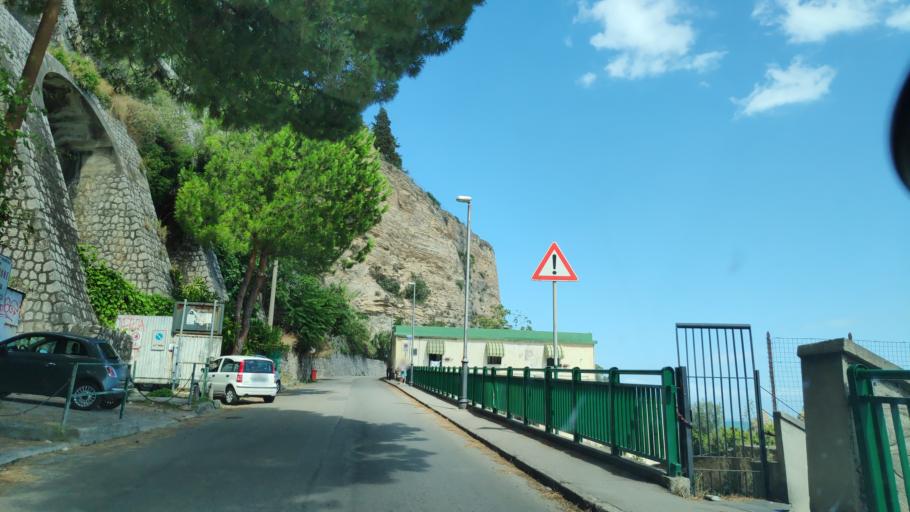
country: IT
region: Campania
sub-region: Provincia di Salerno
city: Vietri sul Mare
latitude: 40.6682
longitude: 14.7263
